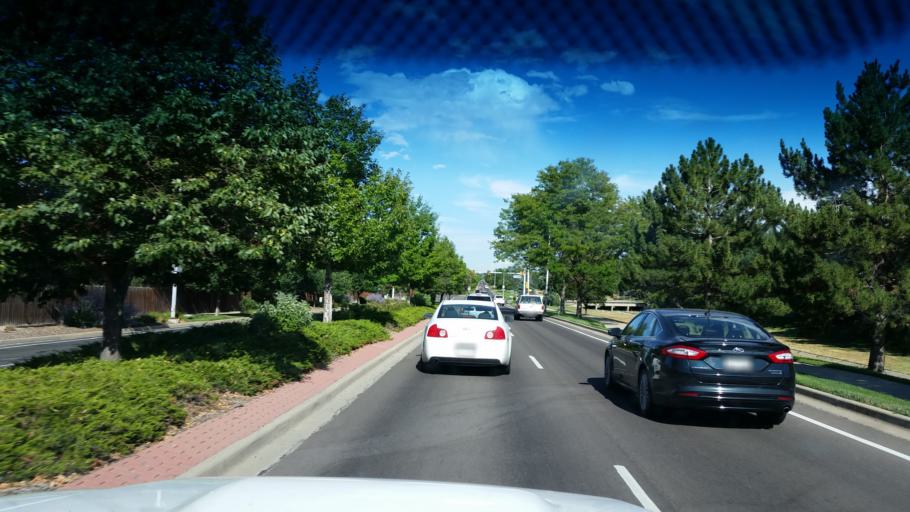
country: US
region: Colorado
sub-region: Broomfield County
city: Broomfield
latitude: 39.9286
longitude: -105.0304
